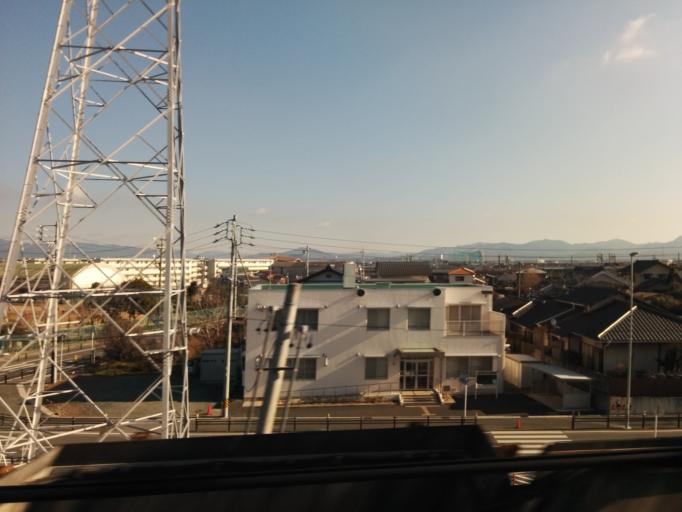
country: JP
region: Aichi
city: Kozakai-cho
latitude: 34.7807
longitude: 137.3664
